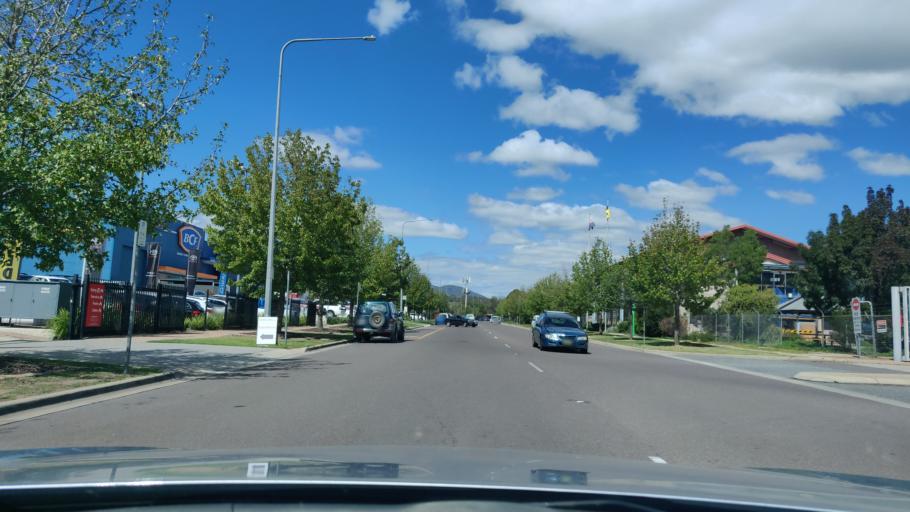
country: AU
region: Australian Capital Territory
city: Macarthur
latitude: -35.4214
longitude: 149.0688
